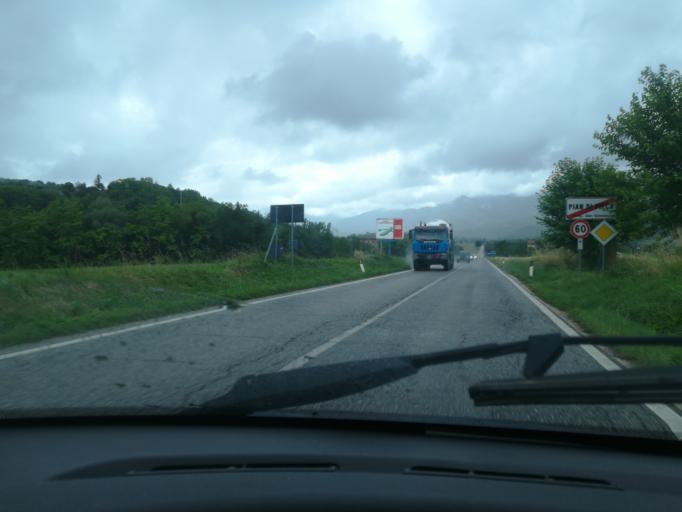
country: IT
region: The Marches
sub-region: Provincia di Macerata
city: Cessapalombo
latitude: 43.0753
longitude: 13.2792
